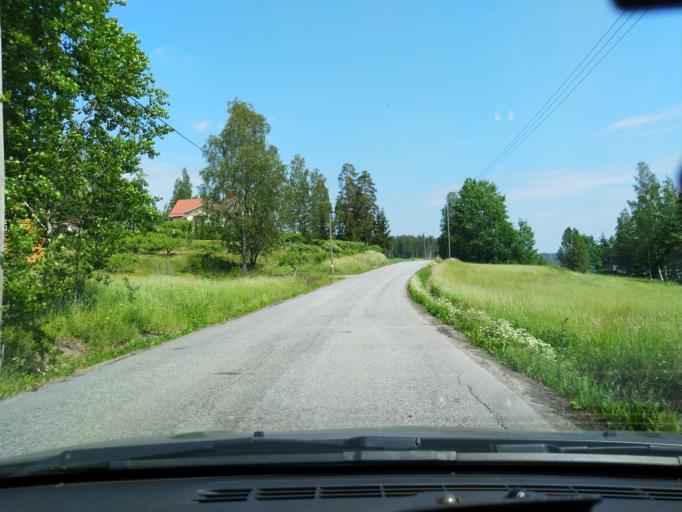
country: FI
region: Uusimaa
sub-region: Helsinki
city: Lohja
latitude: 60.3456
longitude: 24.0878
